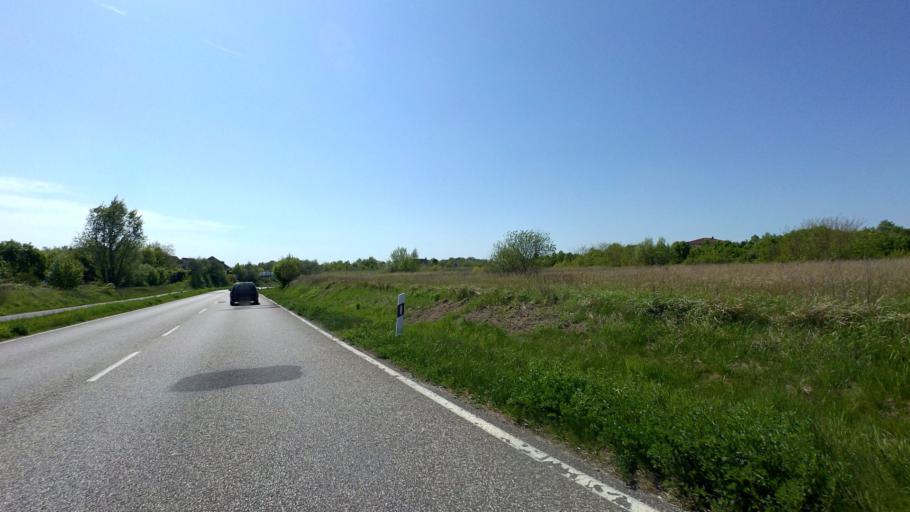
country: DE
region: Brandenburg
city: Konigs Wusterhausen
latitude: 52.3009
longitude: 13.6023
